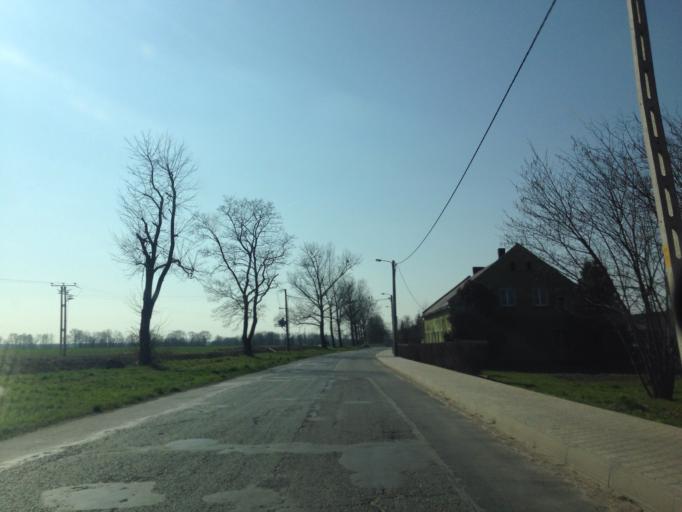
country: PL
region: Lower Silesian Voivodeship
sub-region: Powiat olesnicki
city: Olesnica
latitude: 51.2028
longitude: 17.4504
